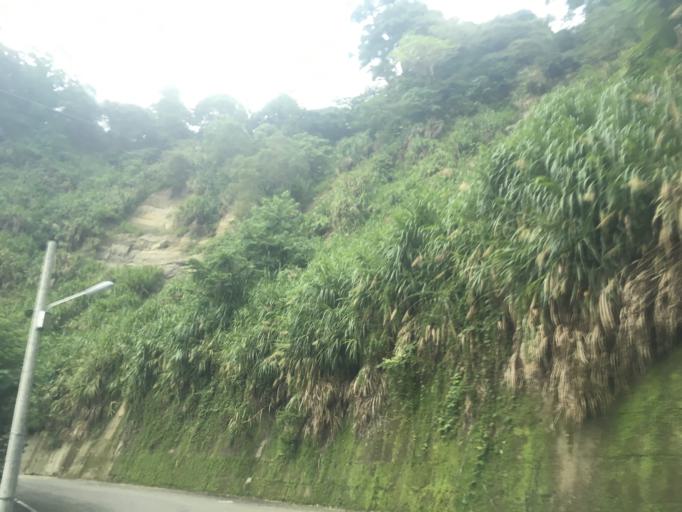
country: TW
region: Taiwan
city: Fengyuan
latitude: 24.1850
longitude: 120.7864
